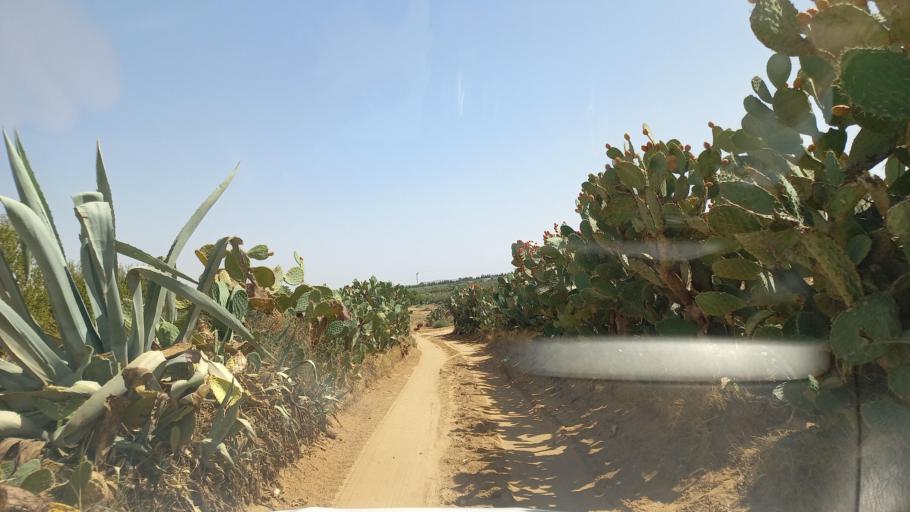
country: TN
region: Al Qasrayn
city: Kasserine
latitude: 35.2377
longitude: 9.0311
